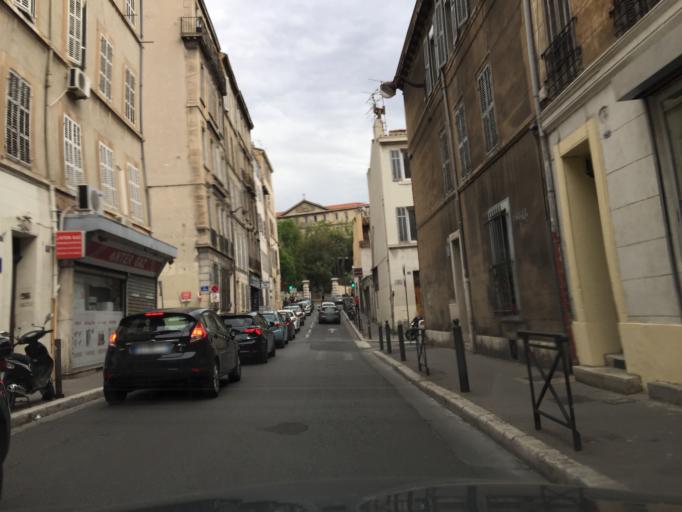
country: FR
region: Provence-Alpes-Cote d'Azur
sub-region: Departement des Bouches-du-Rhone
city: Marseille 04
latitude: 43.3027
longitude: 5.3939
